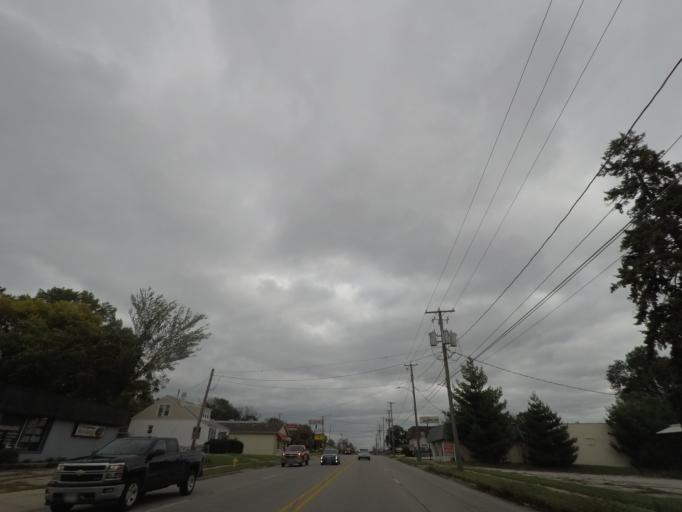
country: US
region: Iowa
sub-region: Warren County
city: Norwalk
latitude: 41.5265
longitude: -93.6315
